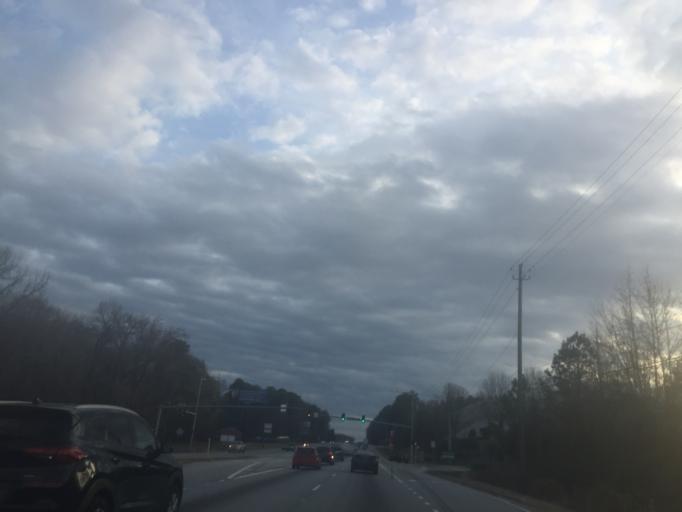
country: US
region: Georgia
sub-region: Clayton County
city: Riverdale
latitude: 33.6039
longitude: -84.4049
